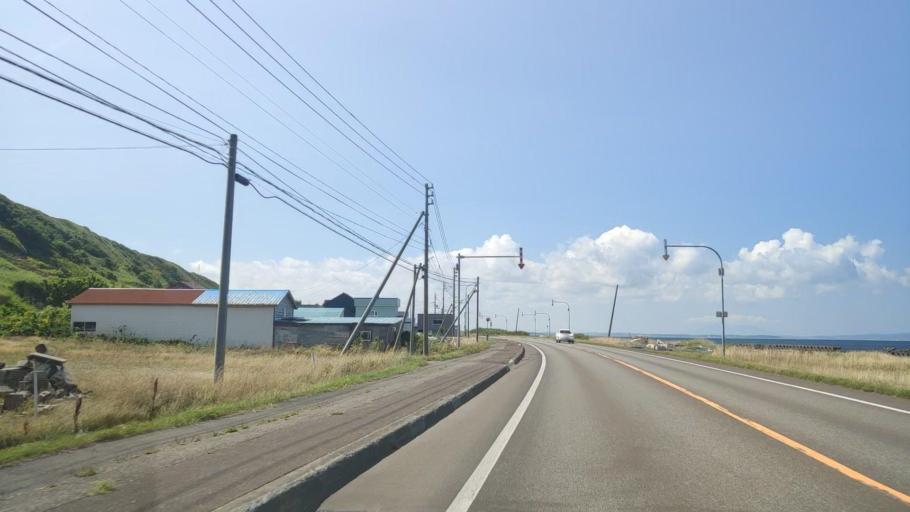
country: JP
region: Hokkaido
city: Makubetsu
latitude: 45.4491
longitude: 141.8715
